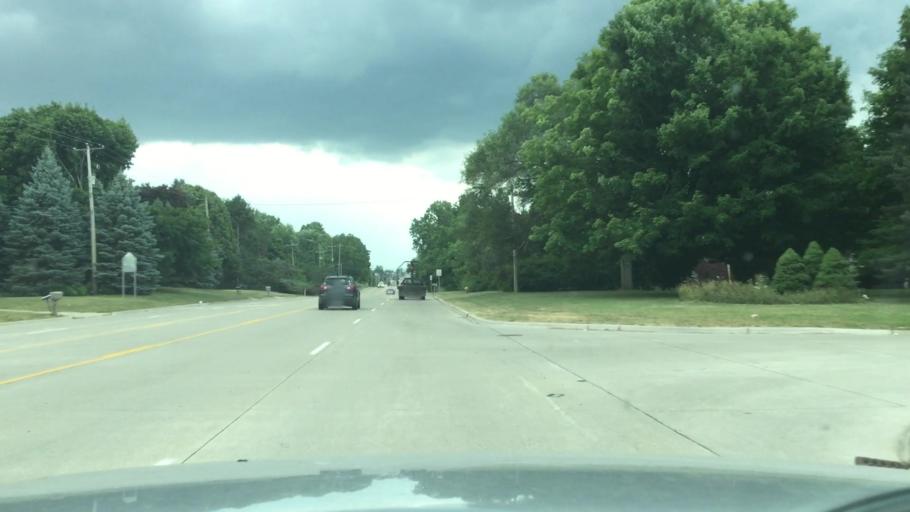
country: US
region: Michigan
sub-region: Genesee County
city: Flint
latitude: 43.0231
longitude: -83.7734
